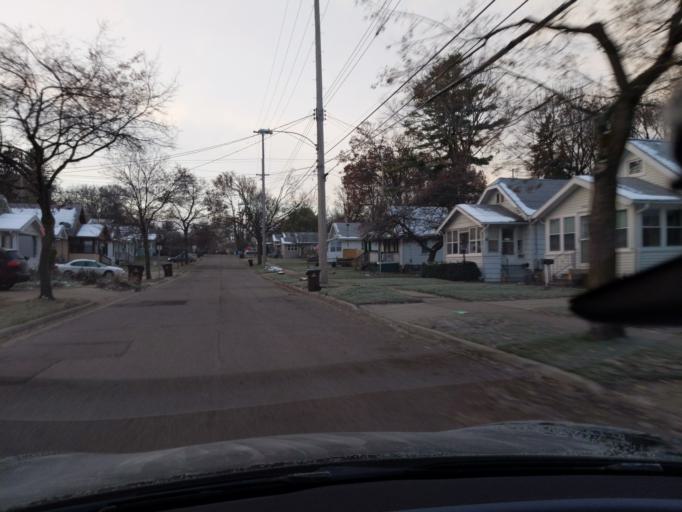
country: US
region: Michigan
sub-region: Ingham County
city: Lansing
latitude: 42.7081
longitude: -84.5522
